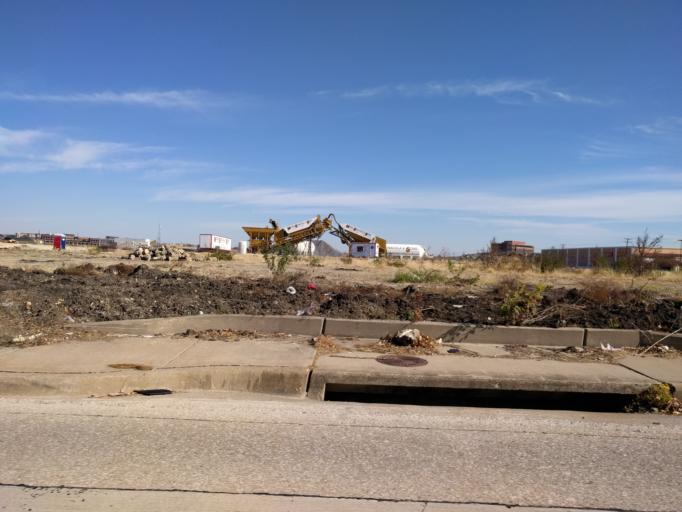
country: US
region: Texas
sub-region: Dallas County
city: Richardson
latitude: 32.9837
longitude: -96.7681
